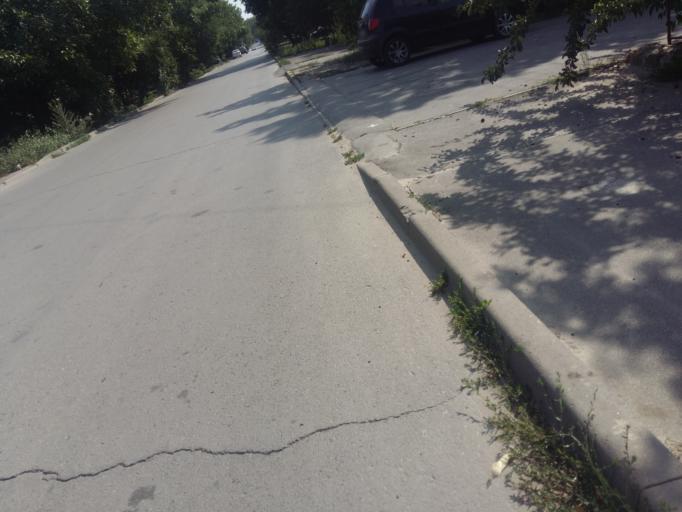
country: RU
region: Rostov
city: Imeni Chkalova
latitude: 47.2788
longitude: 39.7460
